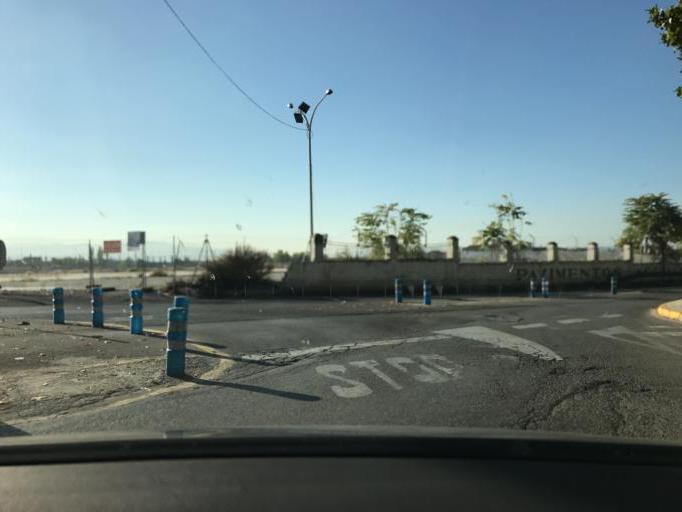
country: ES
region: Andalusia
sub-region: Provincia de Granada
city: Maracena
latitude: 37.2095
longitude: -3.6274
